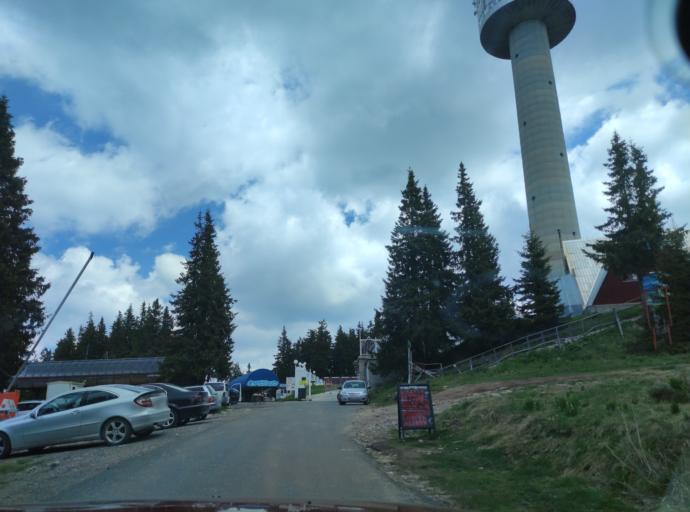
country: BG
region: Smolyan
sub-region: Obshtina Smolyan
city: Smolyan
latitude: 41.6366
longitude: 24.6782
